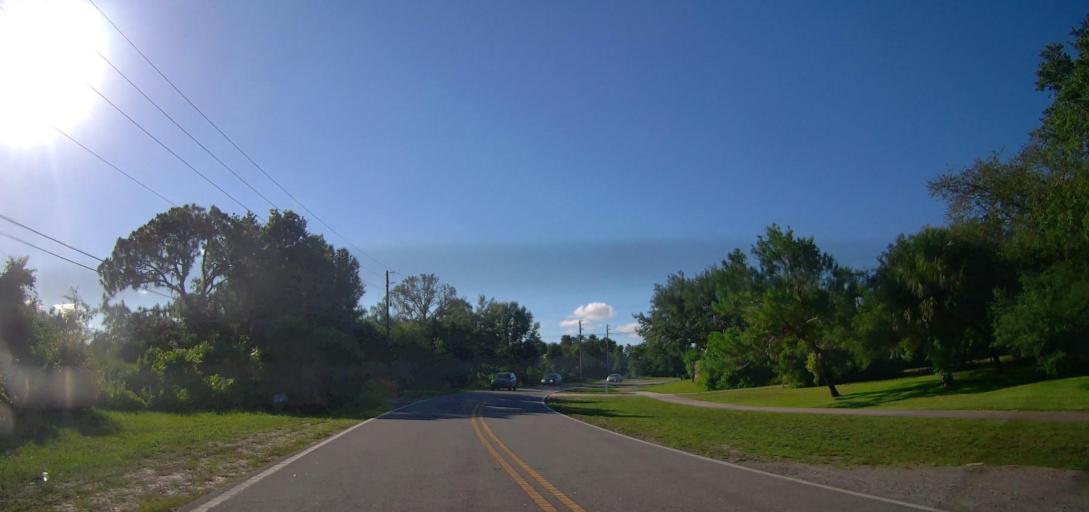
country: US
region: Florida
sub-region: Brevard County
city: Titusville
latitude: 28.5421
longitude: -80.8222
